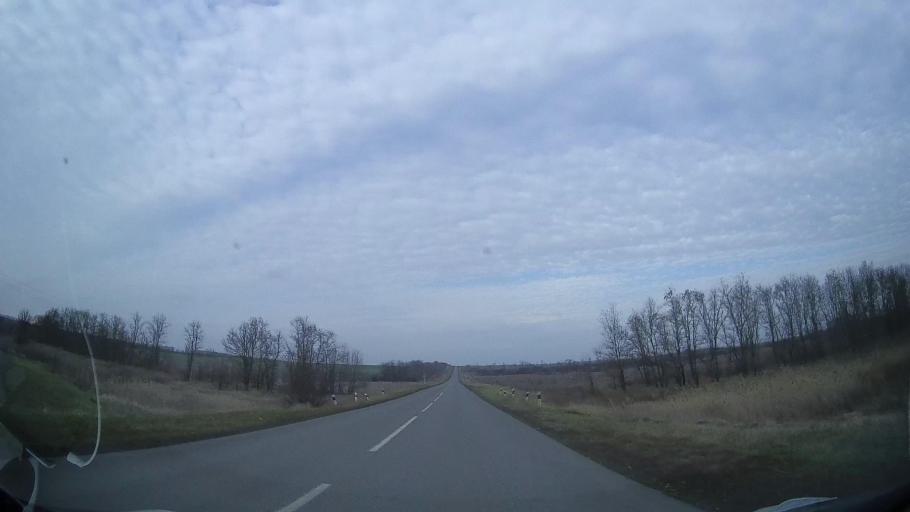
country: RU
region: Rostov
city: Zernograd
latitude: 46.8967
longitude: 40.3389
